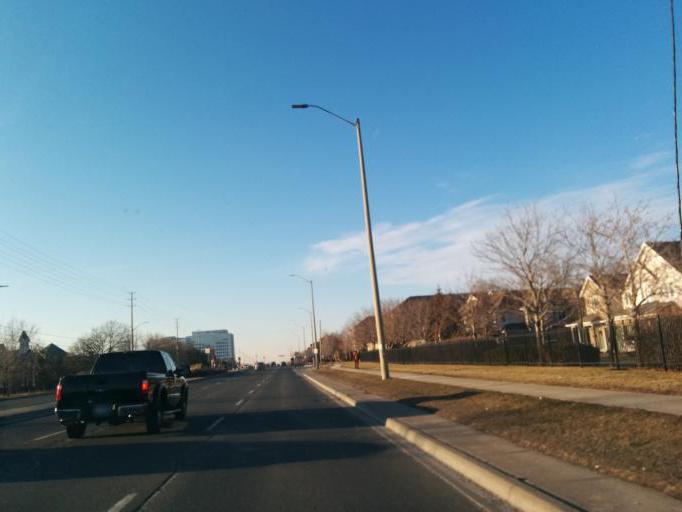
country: CA
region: Ontario
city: Mississauga
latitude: 43.6174
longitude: -79.6671
